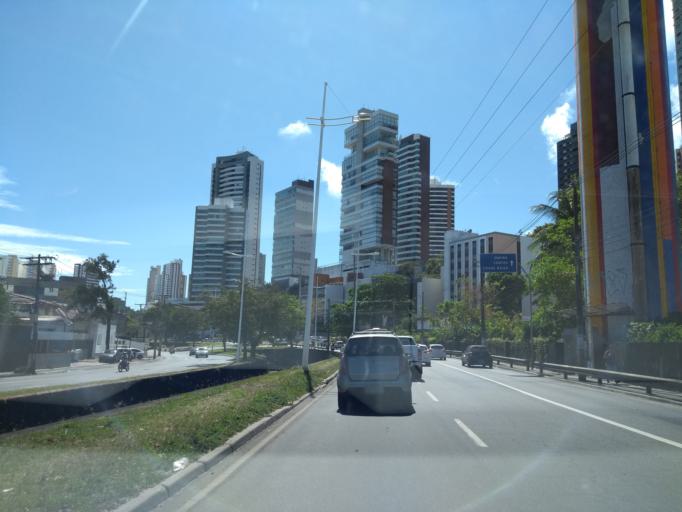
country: BR
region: Bahia
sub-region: Salvador
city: Salvador
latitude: -13.0063
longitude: -38.4886
